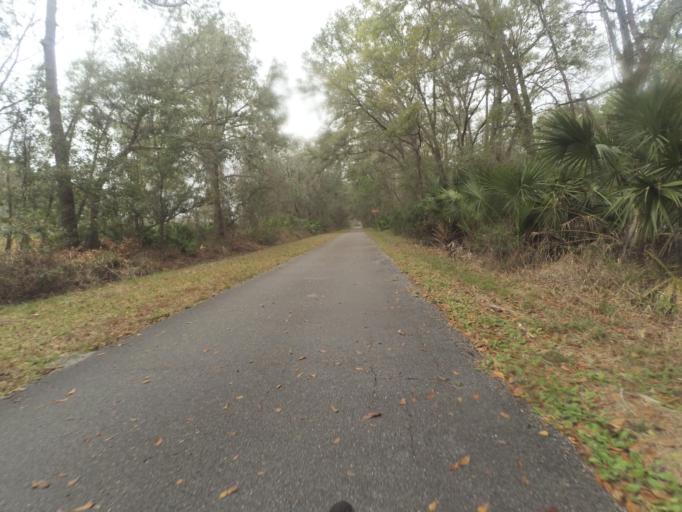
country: US
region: Florida
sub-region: Alachua County
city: Hawthorne
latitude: 29.5920
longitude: -82.1908
